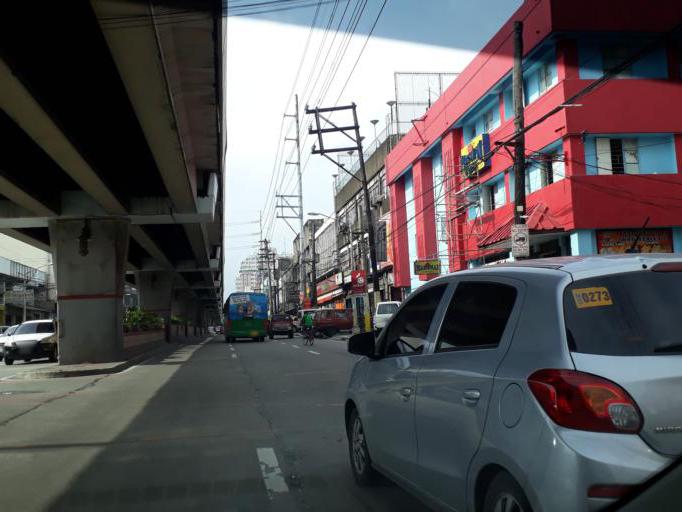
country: PH
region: Calabarzon
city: Del Monte
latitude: 14.6403
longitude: 120.9836
